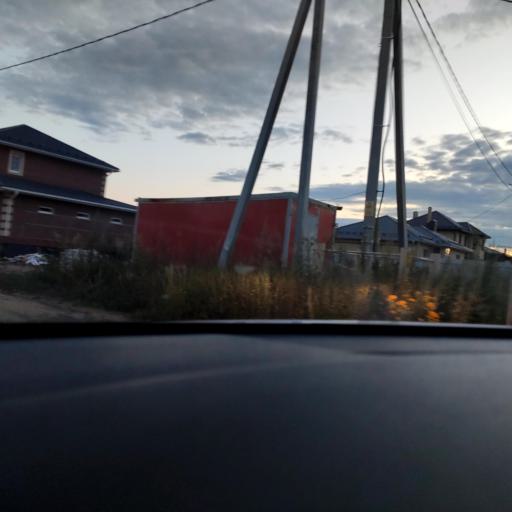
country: RU
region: Tatarstan
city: Stolbishchi
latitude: 55.7235
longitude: 49.3012
